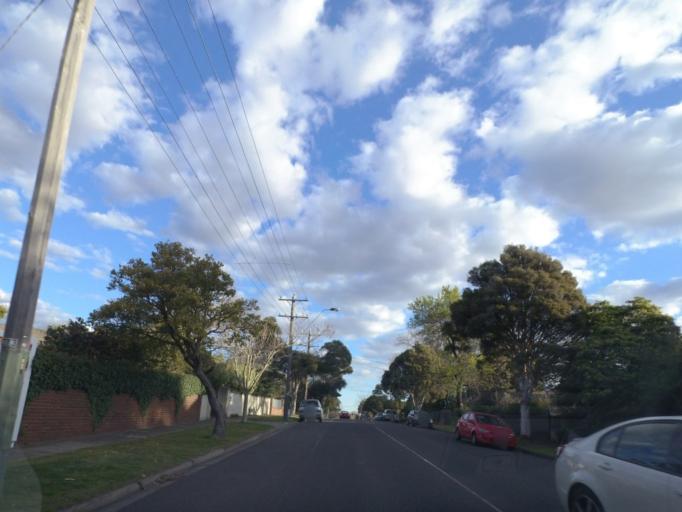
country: AU
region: Victoria
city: Mont Albert
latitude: -37.8132
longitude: 145.0998
